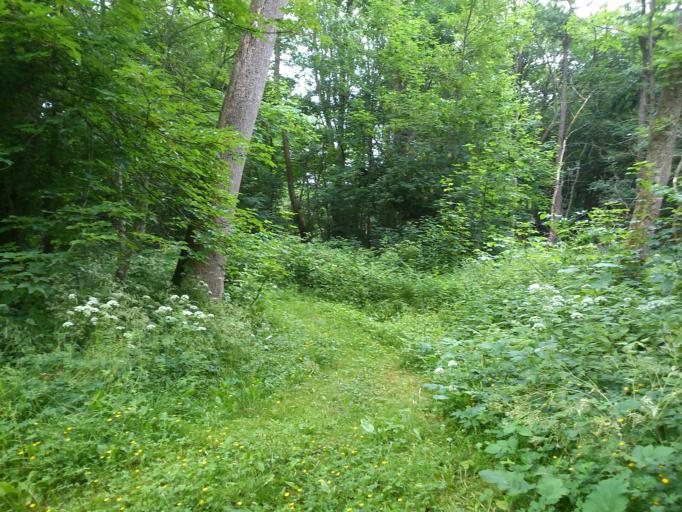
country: DK
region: Central Jutland
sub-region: Ringkobing-Skjern Kommune
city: Skjern
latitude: 55.9989
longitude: 8.4228
